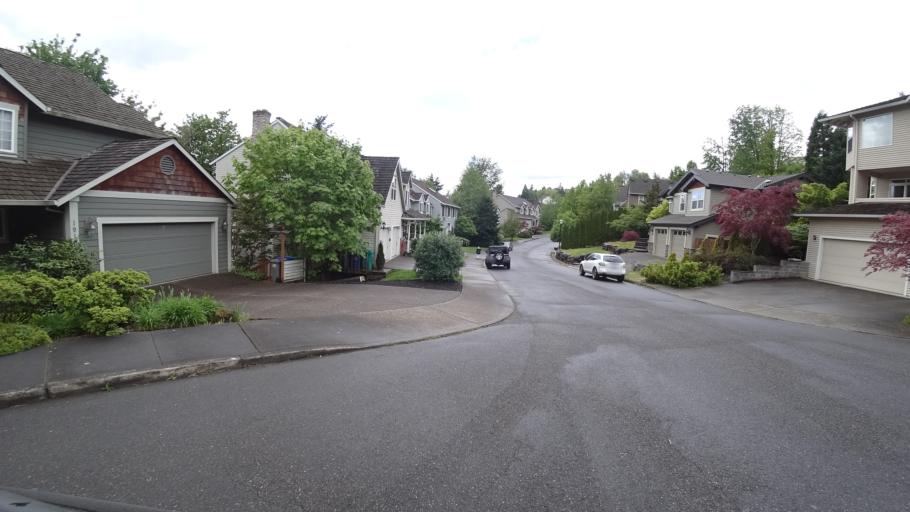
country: US
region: Oregon
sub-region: Washington County
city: West Haven
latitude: 45.5370
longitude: -122.7697
